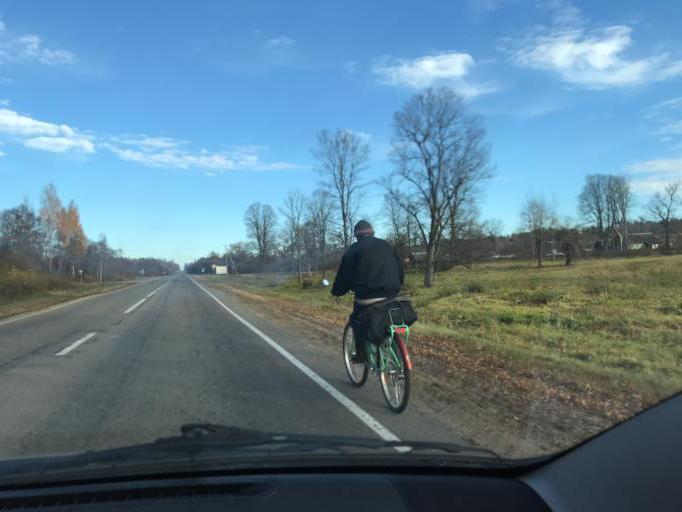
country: BY
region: Vitebsk
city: Haradok
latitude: 55.5248
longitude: 29.9720
